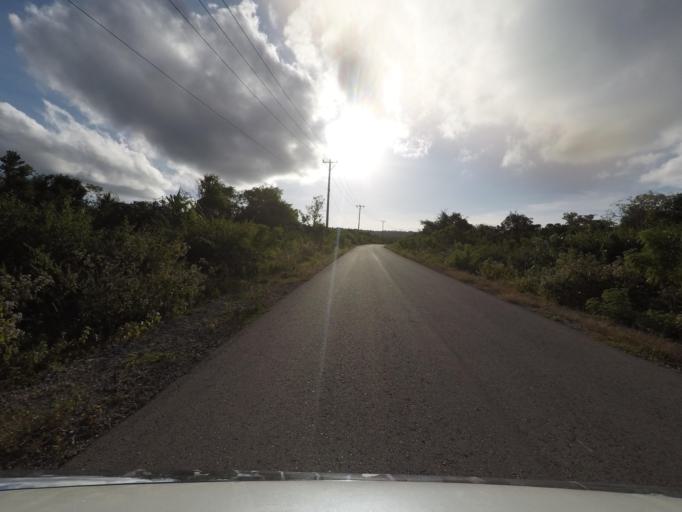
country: TL
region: Lautem
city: Lospalos
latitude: -8.4157
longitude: 127.0016
